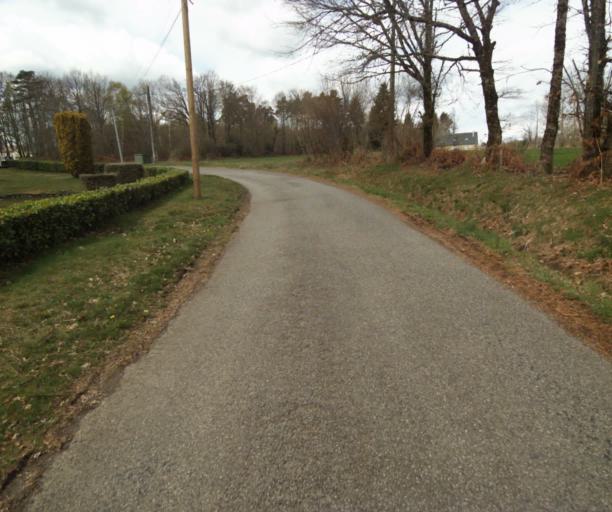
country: FR
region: Limousin
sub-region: Departement de la Correze
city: Laguenne
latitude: 45.2213
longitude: 1.8889
